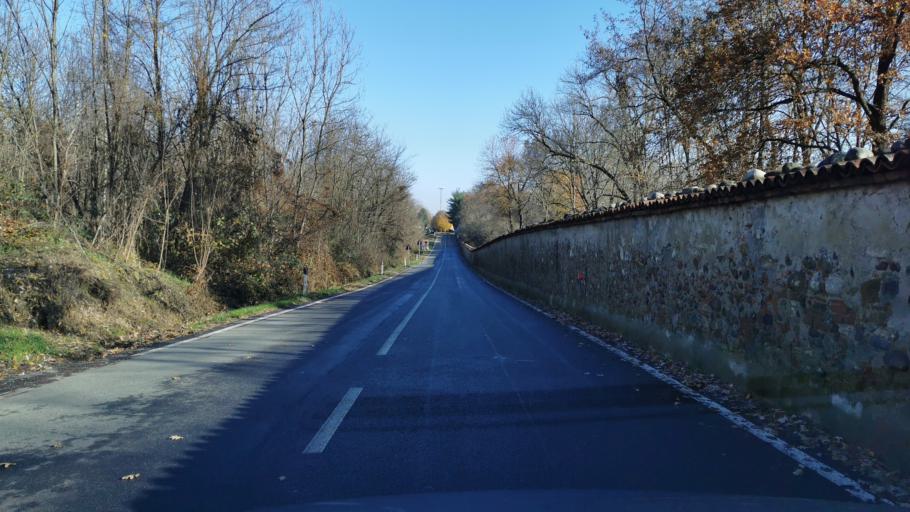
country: IT
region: Piedmont
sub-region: Provincia di Torino
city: Fiano
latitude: 45.2057
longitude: 7.5459
